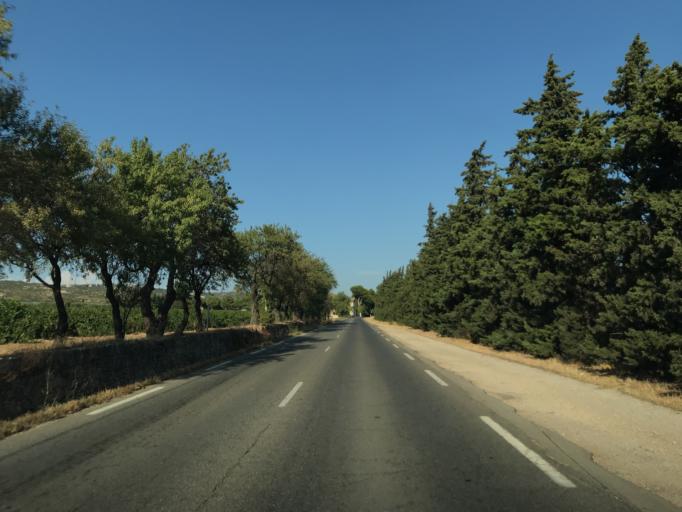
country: FR
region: Provence-Alpes-Cote d'Azur
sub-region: Departement des Bouches-du-Rhone
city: La Fare-les-Oliviers
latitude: 43.5478
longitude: 5.1683
